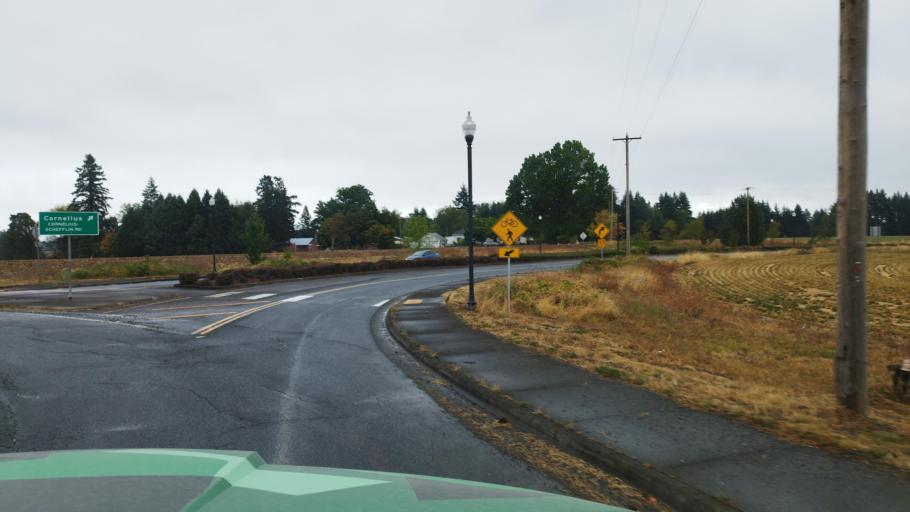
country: US
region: Oregon
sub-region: Washington County
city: Cornelius
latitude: 45.5513
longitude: -123.0639
